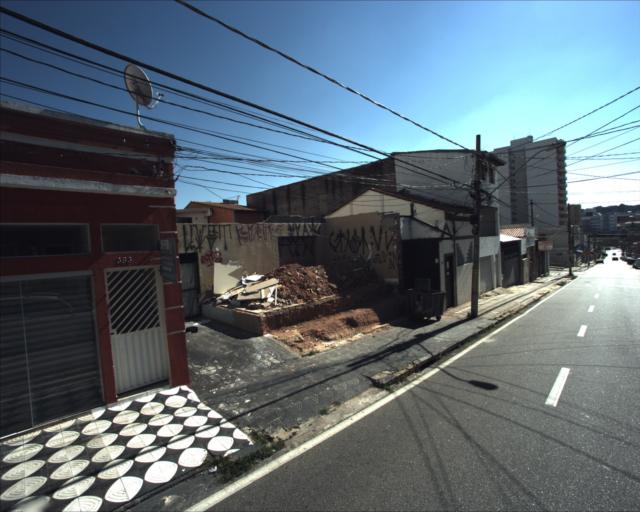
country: BR
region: Sao Paulo
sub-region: Sorocaba
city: Sorocaba
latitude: -23.4983
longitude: -47.4625
